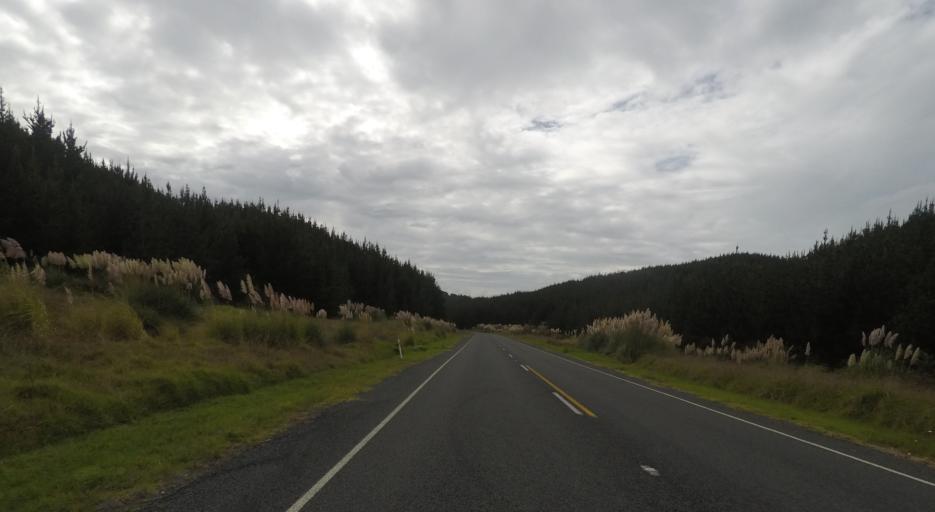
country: NZ
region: Auckland
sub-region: Auckland
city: Rothesay Bay
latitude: -36.6541
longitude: 174.7023
